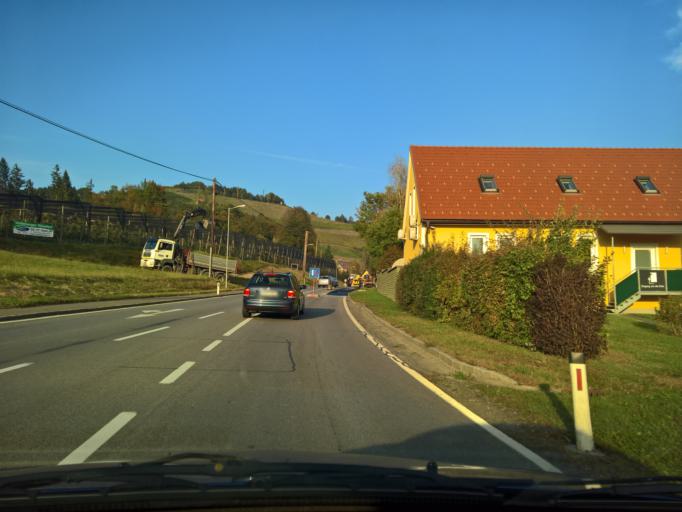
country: AT
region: Styria
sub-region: Politischer Bezirk Leibnitz
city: Seggauberg
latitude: 46.7759
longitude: 15.5078
